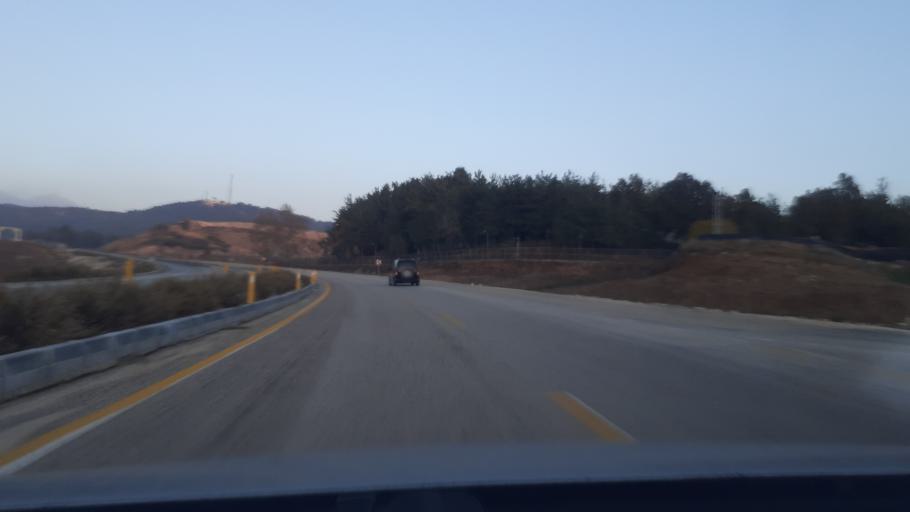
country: TR
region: Hatay
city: Yayladagi
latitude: 35.8909
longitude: 36.0915
